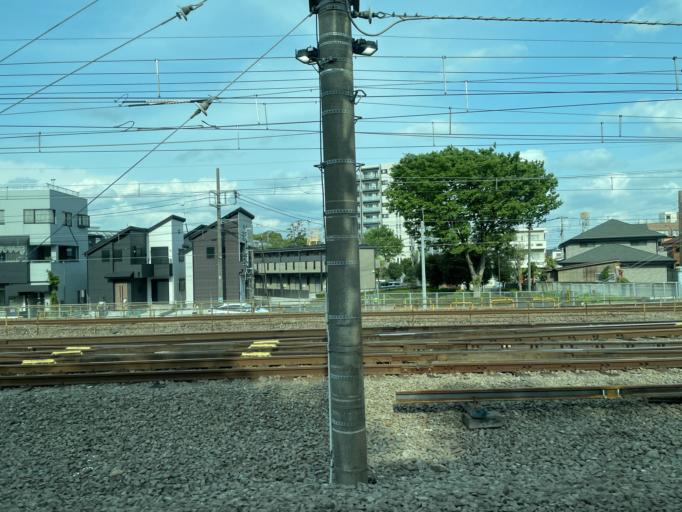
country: JP
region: Tokyo
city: Kokubunji
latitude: 35.6642
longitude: 139.4776
